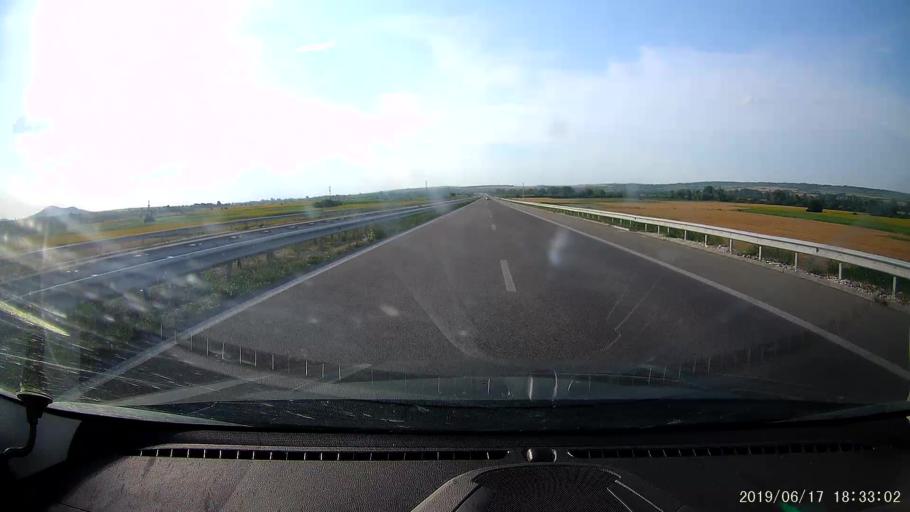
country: BG
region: Khaskovo
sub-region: Obshtina Dimitrovgrad
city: Dimitrovgrad
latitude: 42.0710
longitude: 25.4664
